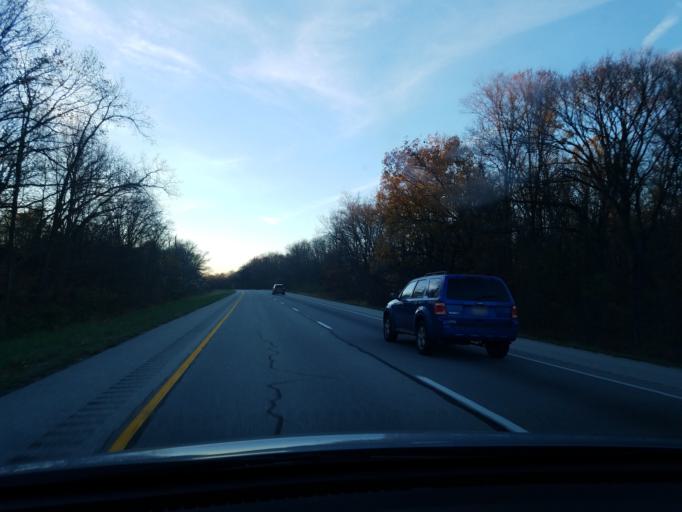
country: US
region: Indiana
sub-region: Posey County
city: Poseyville
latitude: 38.1940
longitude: -87.8421
